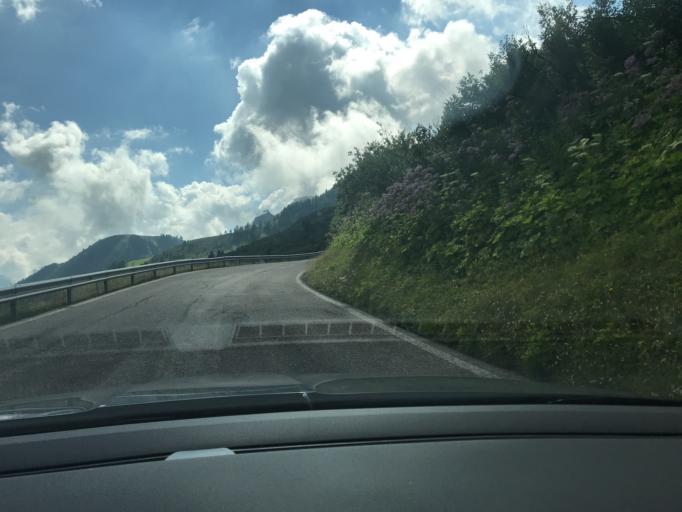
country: IT
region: Trentino-Alto Adige
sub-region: Provincia di Trento
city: Canazei
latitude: 46.4850
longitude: 11.8401
